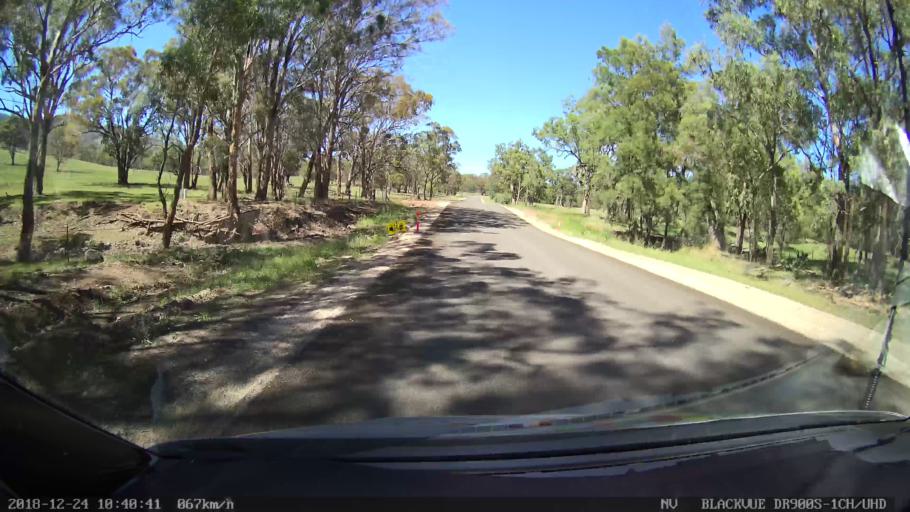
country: AU
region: New South Wales
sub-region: Upper Hunter Shire
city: Merriwa
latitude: -31.8633
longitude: 150.4652
